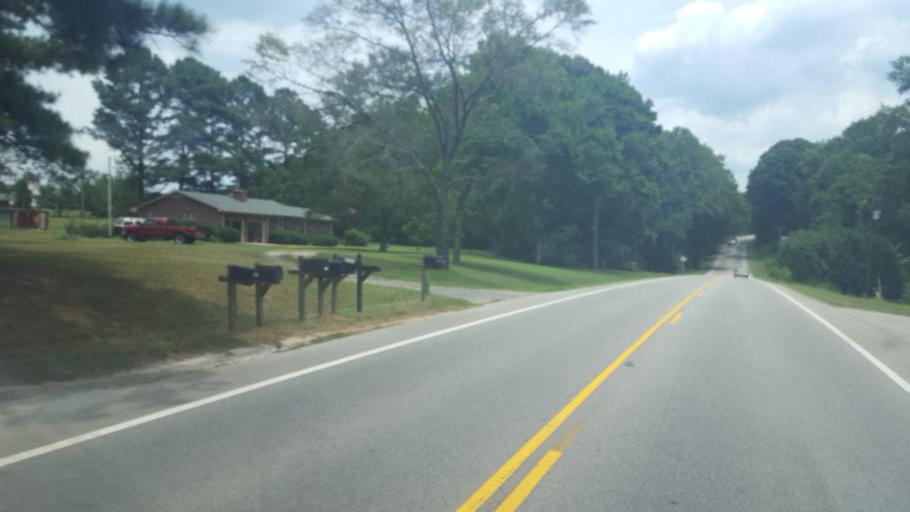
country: US
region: South Carolina
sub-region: York County
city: Newport
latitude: 34.9715
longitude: -81.1612
